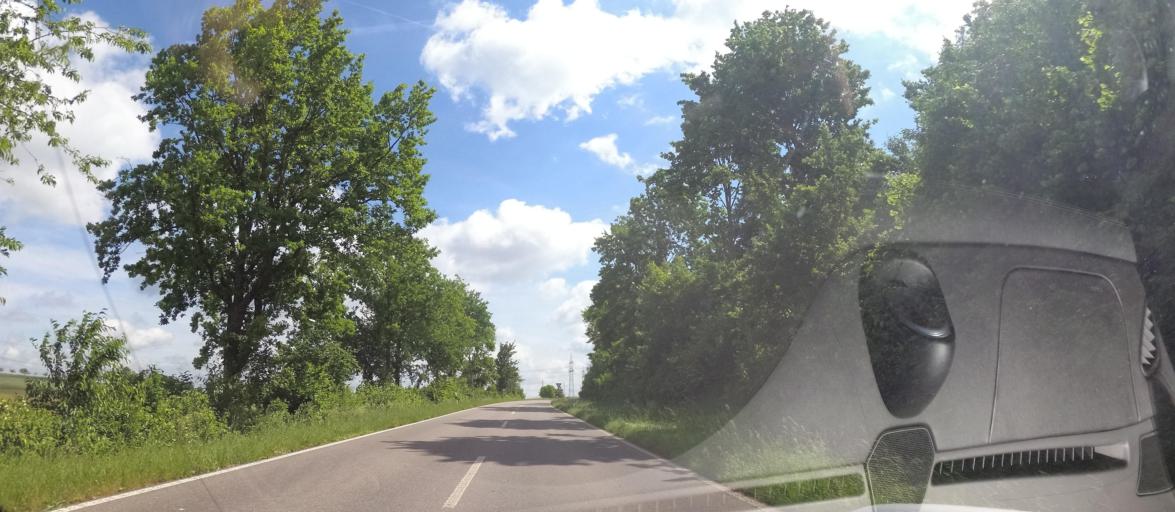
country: DE
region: Baden-Wuerttemberg
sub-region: Karlsruhe Region
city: Bretten
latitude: 49.0757
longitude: 8.7196
